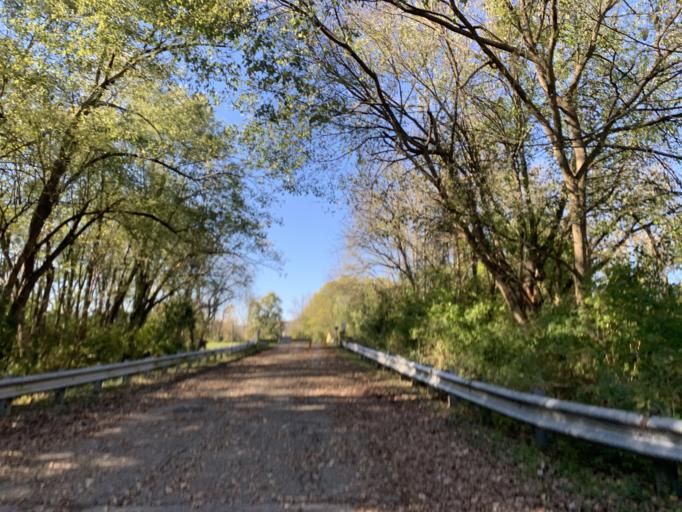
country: US
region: Kentucky
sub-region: Jefferson County
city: Saint Dennis
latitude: 38.1941
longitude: -85.8772
